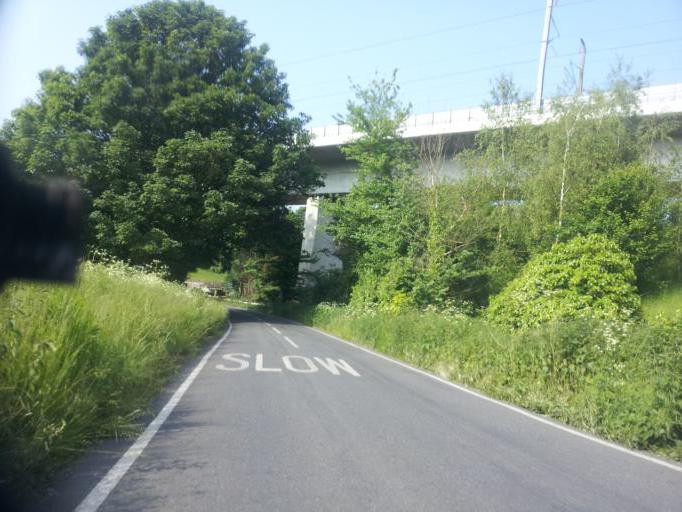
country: GB
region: England
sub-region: Medway
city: Cuxton
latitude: 51.3702
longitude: 0.4792
